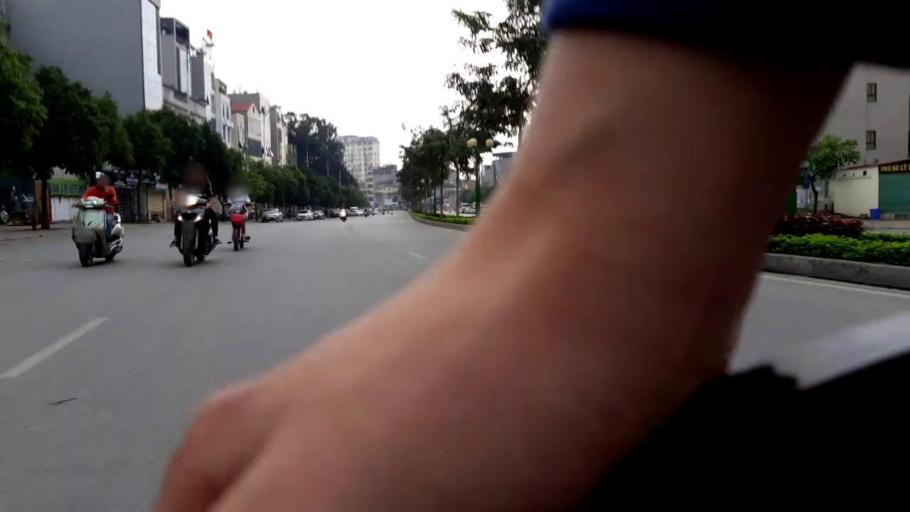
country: VN
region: Ha Noi
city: Cau Giay
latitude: 21.0367
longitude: 105.7979
